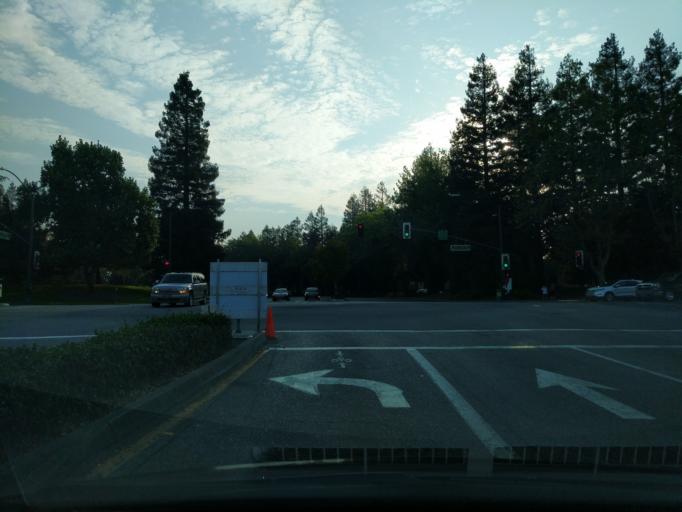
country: US
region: California
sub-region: Santa Clara County
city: Mountain View
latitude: 37.4238
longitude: -122.0897
